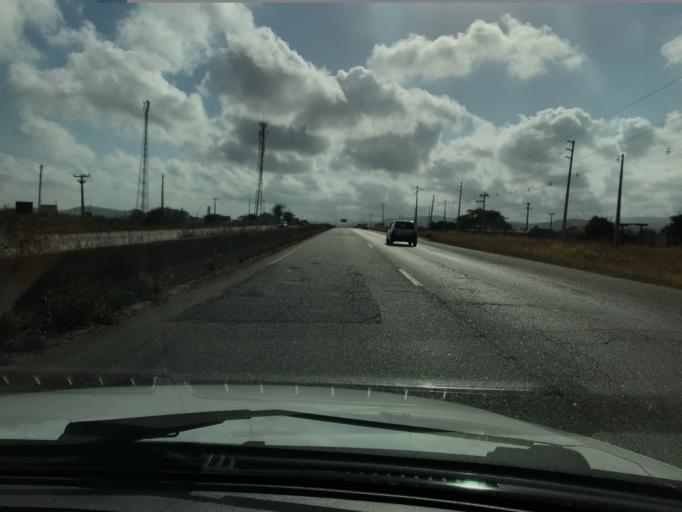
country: BR
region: Pernambuco
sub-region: Gravata
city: Gravata
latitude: -8.2172
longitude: -35.6534
